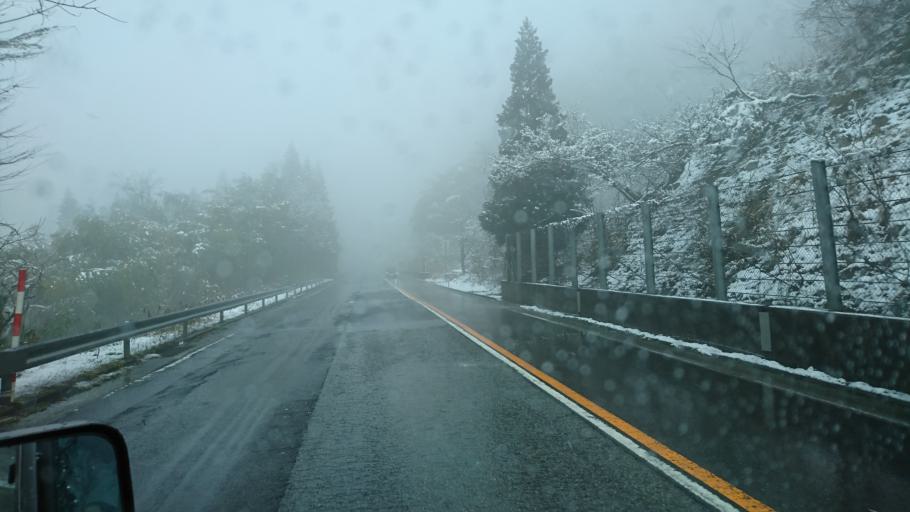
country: JP
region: Hyogo
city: Toyooka
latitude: 35.4946
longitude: 134.5400
